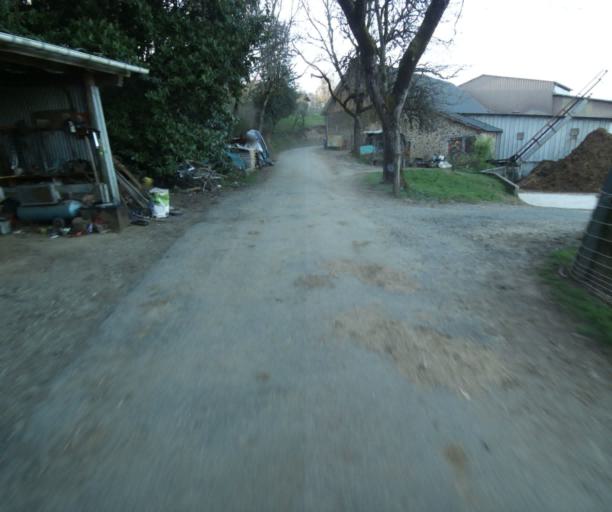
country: FR
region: Limousin
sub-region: Departement de la Correze
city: Seilhac
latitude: 45.3430
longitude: 1.7245
